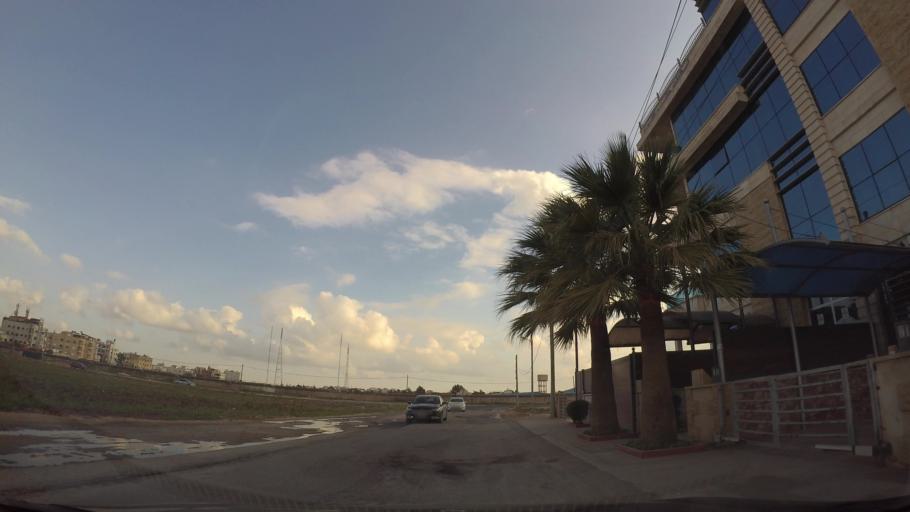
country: JO
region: Amman
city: Al Bunayyat ash Shamaliyah
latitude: 31.9095
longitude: 35.8781
